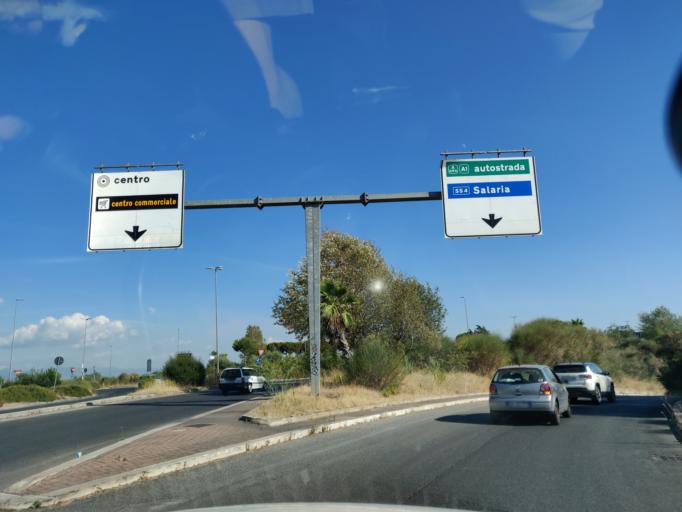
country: IT
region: Latium
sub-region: Citta metropolitana di Roma Capitale
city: Colle Verde
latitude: 41.9687
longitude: 12.5388
